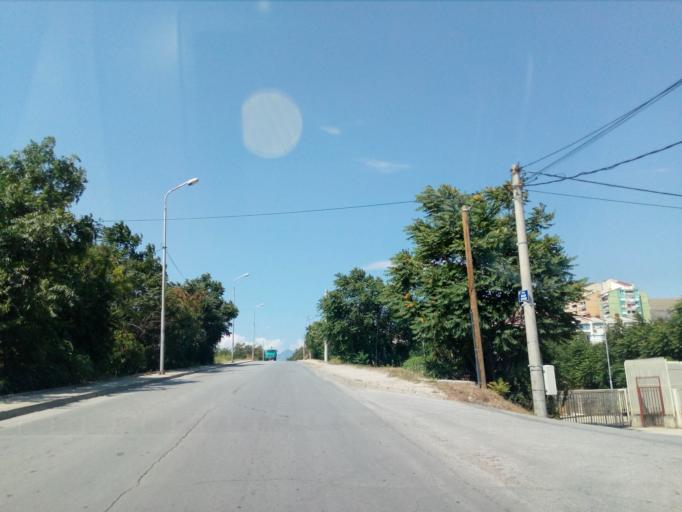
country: MK
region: Veles
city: Veles
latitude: 41.7196
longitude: 21.7656
